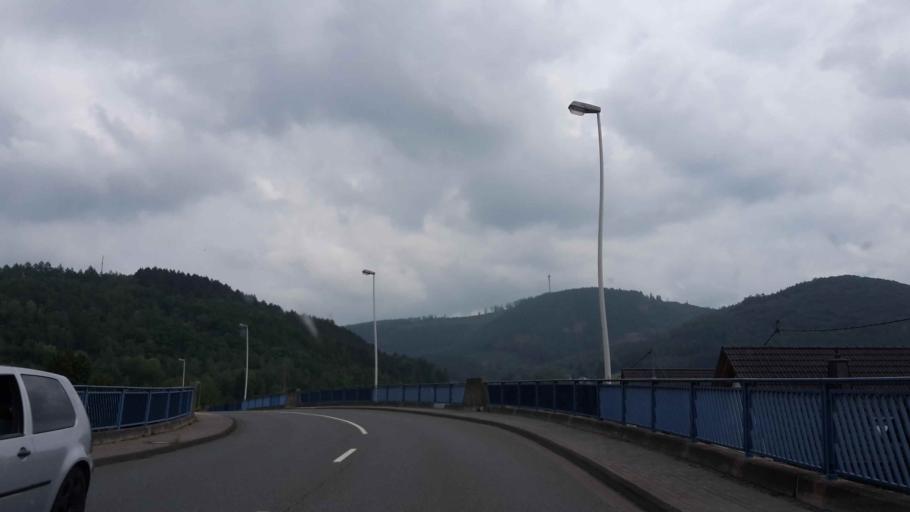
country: DE
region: North Rhine-Westphalia
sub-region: Regierungsbezirk Arnsberg
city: Lennestadt
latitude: 51.1258
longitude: 8.0568
